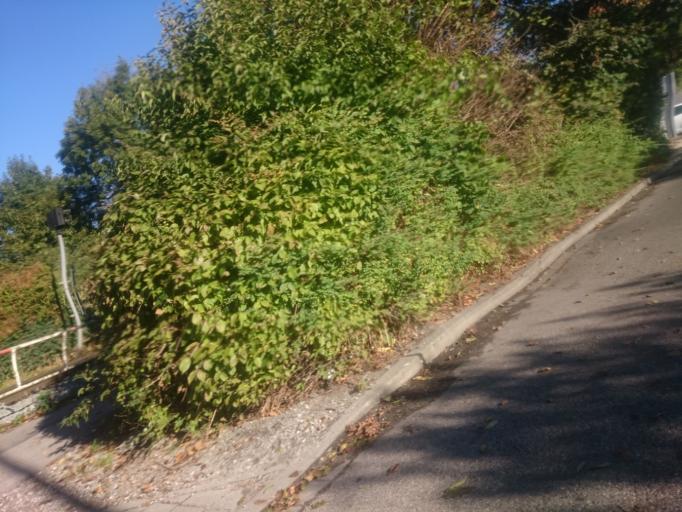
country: DE
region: Bavaria
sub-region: Swabia
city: Augsburg
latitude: 48.3651
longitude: 10.9242
